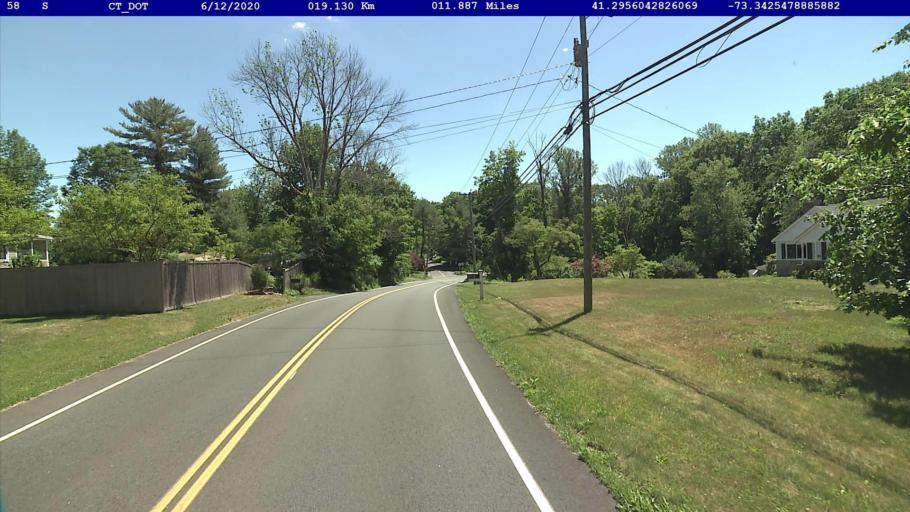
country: US
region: Connecticut
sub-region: Fairfield County
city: Georgetown
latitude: 41.2956
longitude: -73.3426
